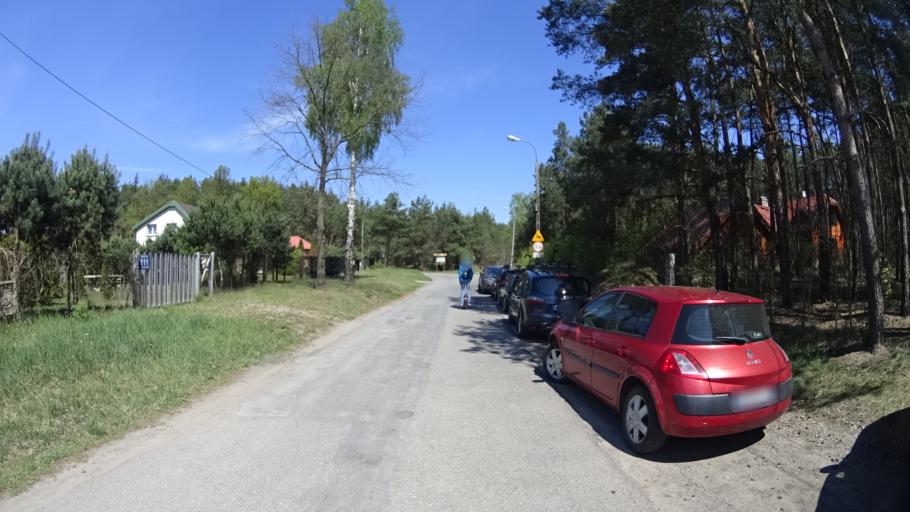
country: PL
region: Masovian Voivodeship
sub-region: Powiat warszawski zachodni
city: Truskaw
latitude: 52.2830
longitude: 20.7444
